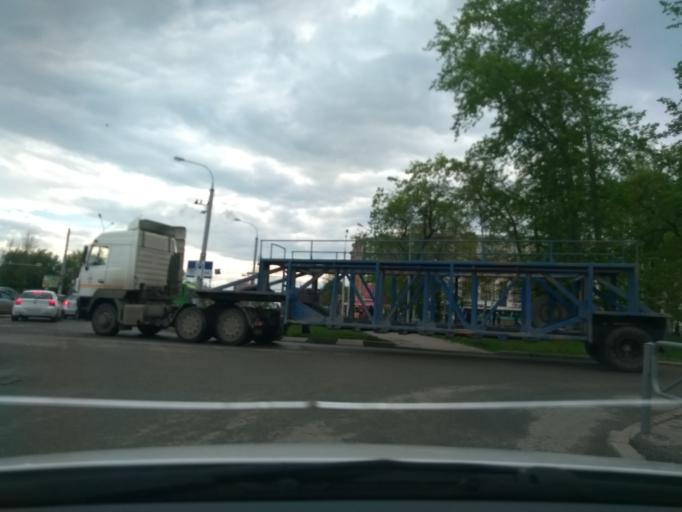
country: RU
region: Perm
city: Perm
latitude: 57.9861
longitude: 56.2601
